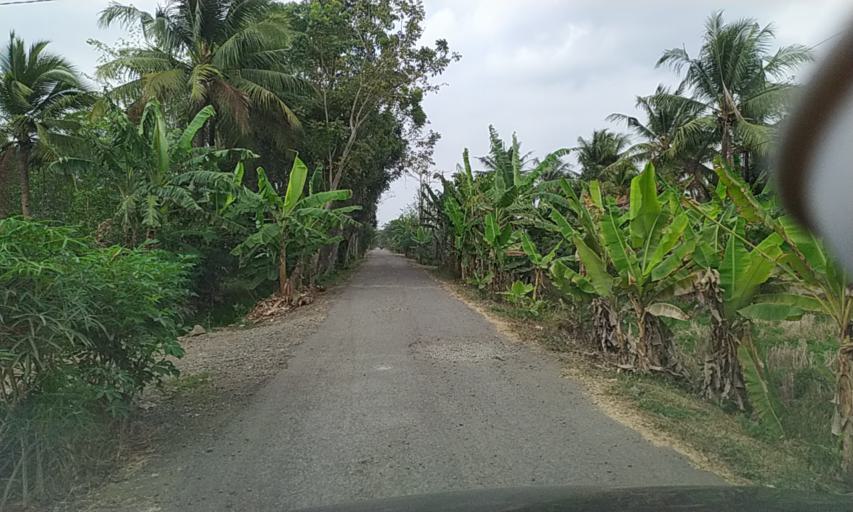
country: ID
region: Central Java
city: Karanganyar
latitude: -7.6661
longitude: 108.9114
